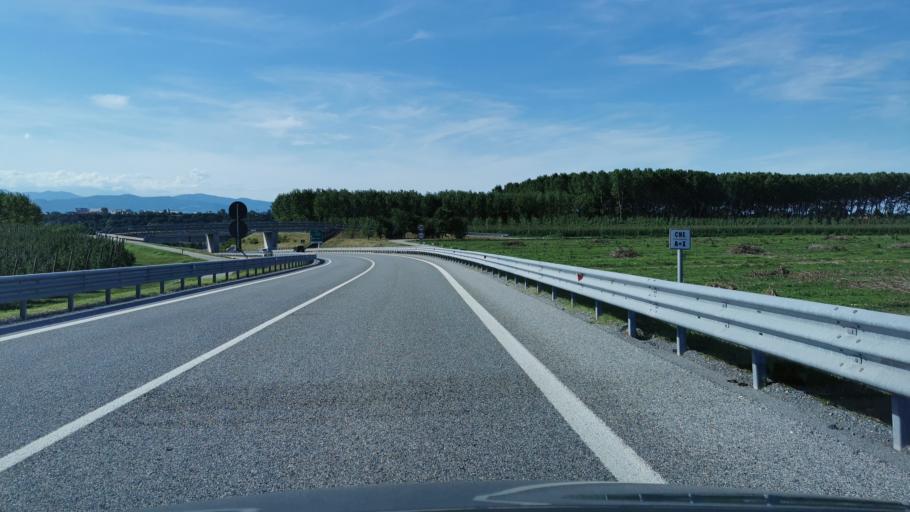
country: IT
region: Piedmont
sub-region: Provincia di Cuneo
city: Castelletto Stura
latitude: 44.4173
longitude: 7.5956
